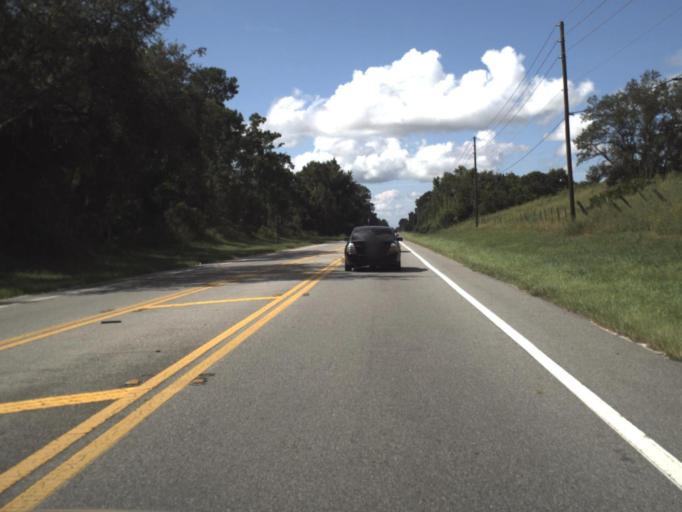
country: US
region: Florida
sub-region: Polk County
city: Loughman
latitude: 28.2304
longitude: -81.5632
